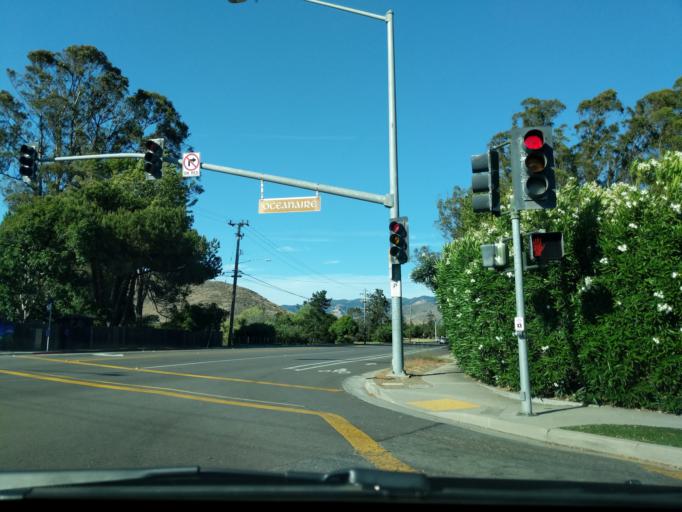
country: US
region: California
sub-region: San Luis Obispo County
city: San Luis Obispo
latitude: 35.2593
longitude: -120.6842
